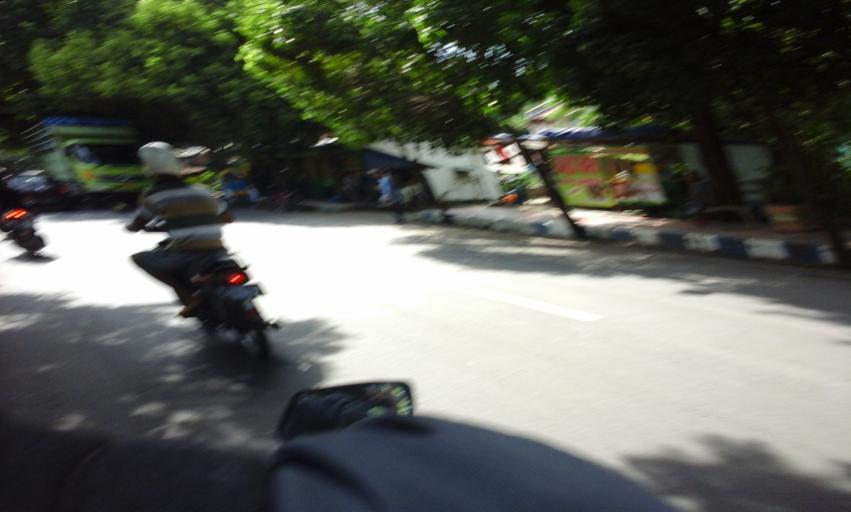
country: ID
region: East Java
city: Cungking
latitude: -8.2155
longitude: 114.3563
